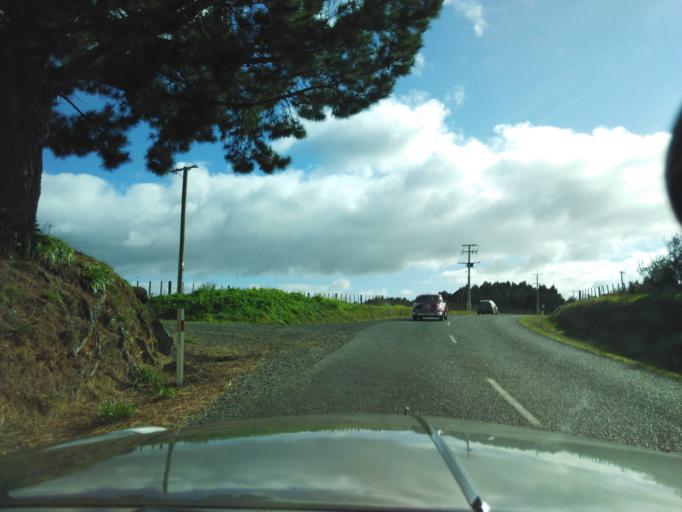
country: NZ
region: Auckland
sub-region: Auckland
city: Red Hill
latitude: -37.0719
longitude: 175.0713
